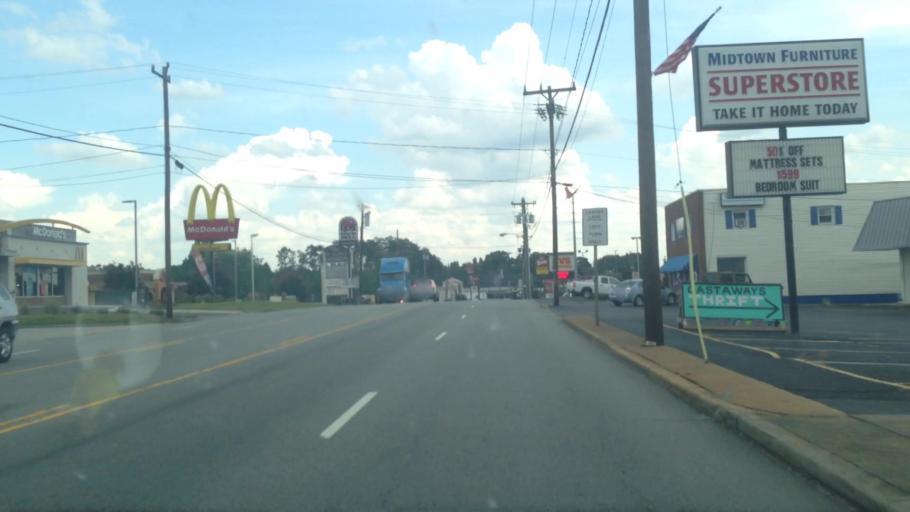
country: US
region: North Carolina
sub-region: Rockingham County
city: Madison
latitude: 36.3969
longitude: -79.9699
